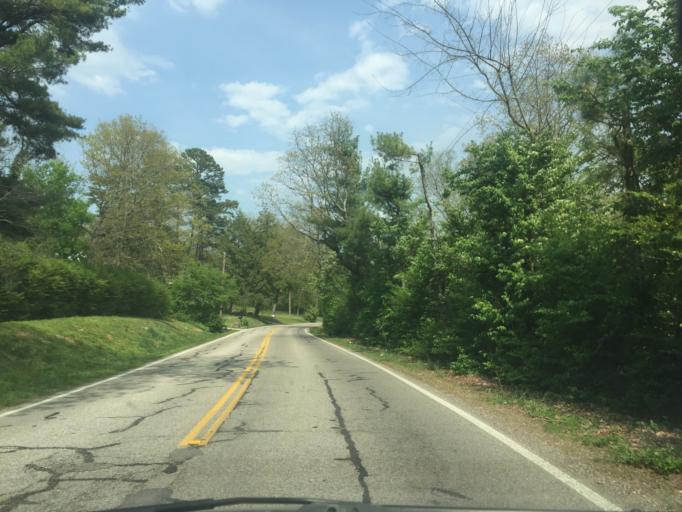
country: US
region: Tennessee
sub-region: Hamilton County
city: Signal Mountain
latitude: 35.1212
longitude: -85.3517
